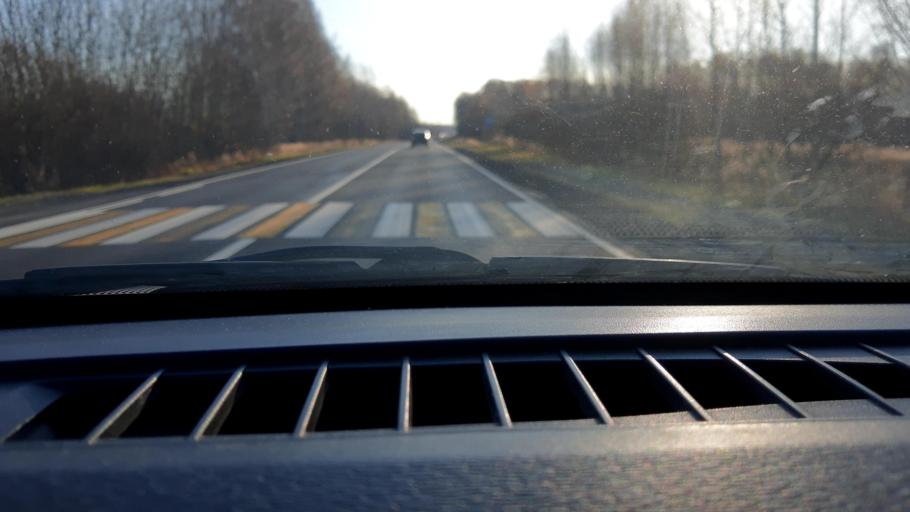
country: RU
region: Nizjnij Novgorod
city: Novaya Balakhna
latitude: 56.5913
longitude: 43.6597
